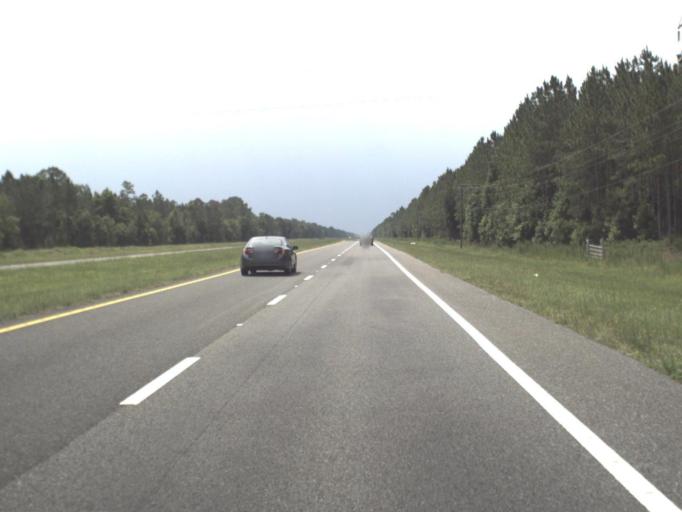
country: US
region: Florida
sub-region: Levy County
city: Chiefland
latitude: 29.3935
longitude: -82.8091
